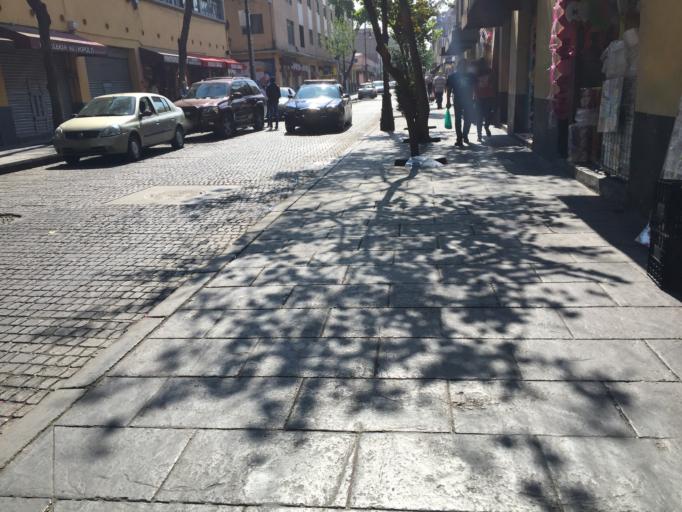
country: MX
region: Mexico City
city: Mexico City
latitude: 19.4278
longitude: -99.1274
